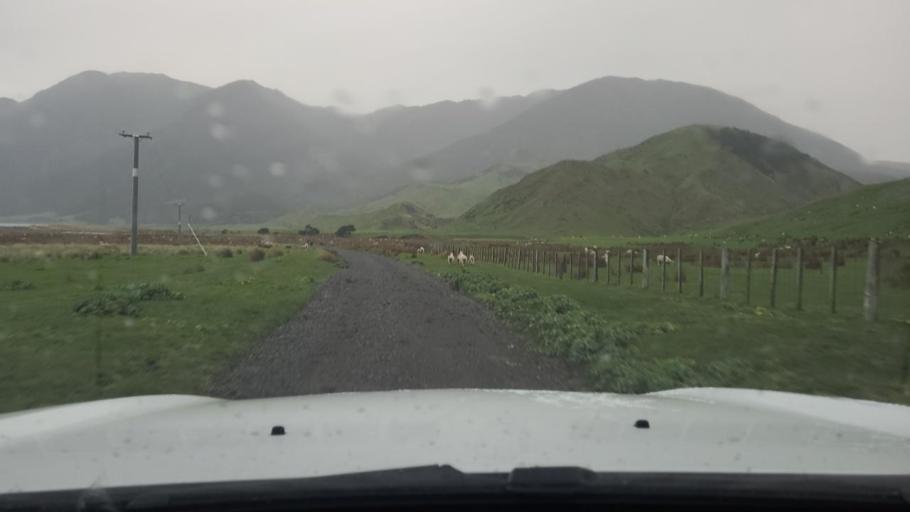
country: NZ
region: Wellington
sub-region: South Wairarapa District
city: Waipawa
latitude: -41.5664
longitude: 175.3873
